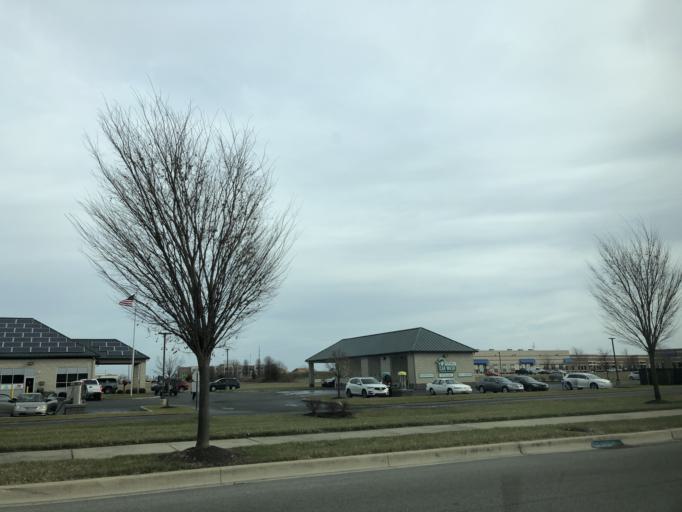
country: US
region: Delaware
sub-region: New Castle County
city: Middletown
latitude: 39.4377
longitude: -75.7516
